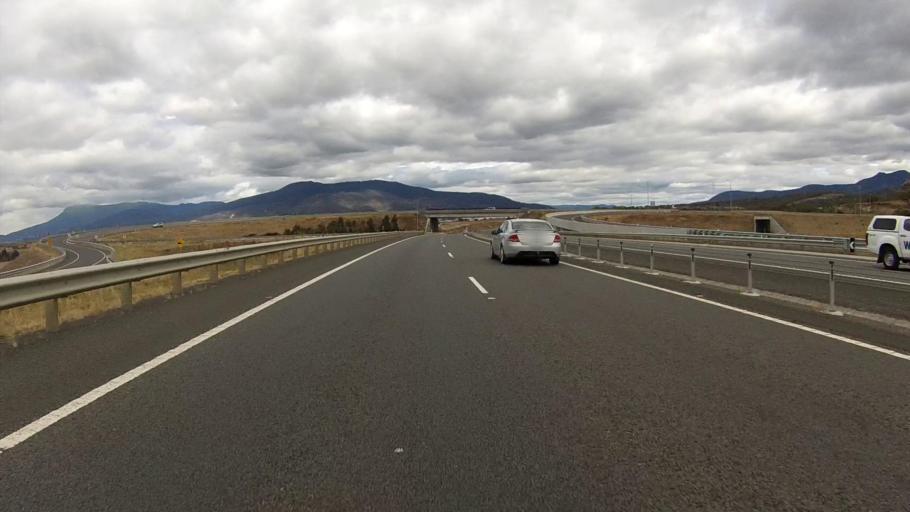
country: AU
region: Tasmania
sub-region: Brighton
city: Bridgewater
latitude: -42.7124
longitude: 147.2471
